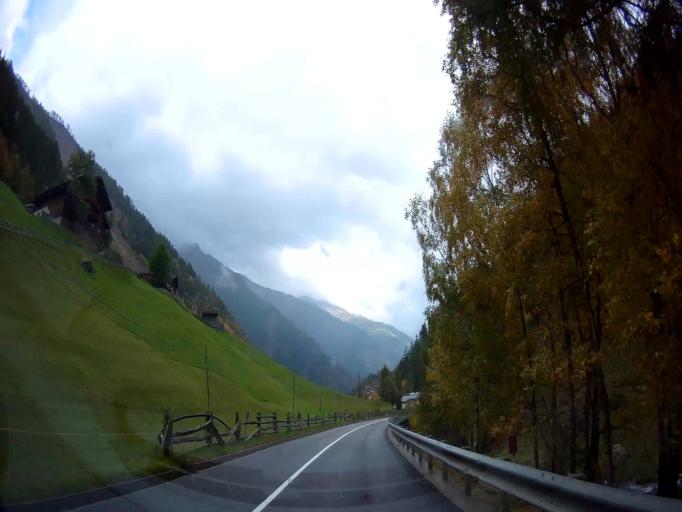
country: IT
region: Trentino-Alto Adige
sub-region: Bolzano
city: Senales
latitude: 46.7128
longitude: 10.8937
